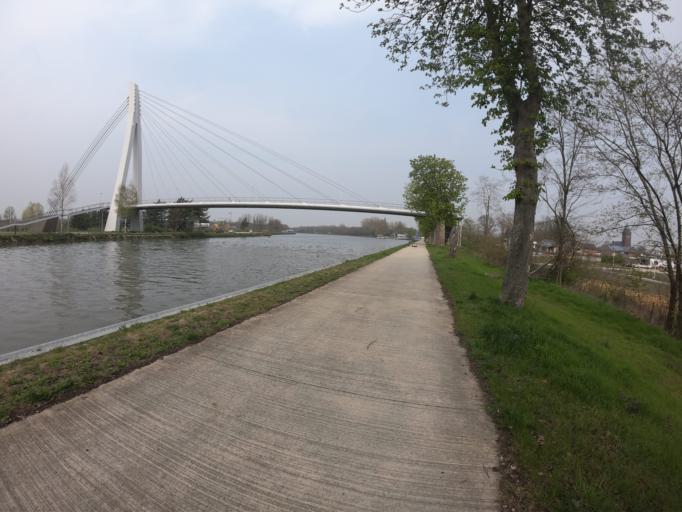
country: BE
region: Flanders
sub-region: Provincie Limburg
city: Maasmechelen
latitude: 51.0122
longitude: 5.7163
